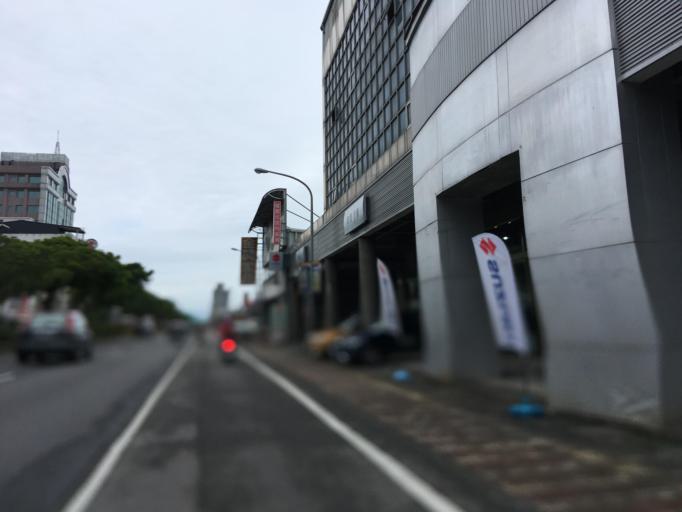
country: TW
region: Taiwan
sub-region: Yilan
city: Yilan
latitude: 24.7019
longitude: 121.7699
